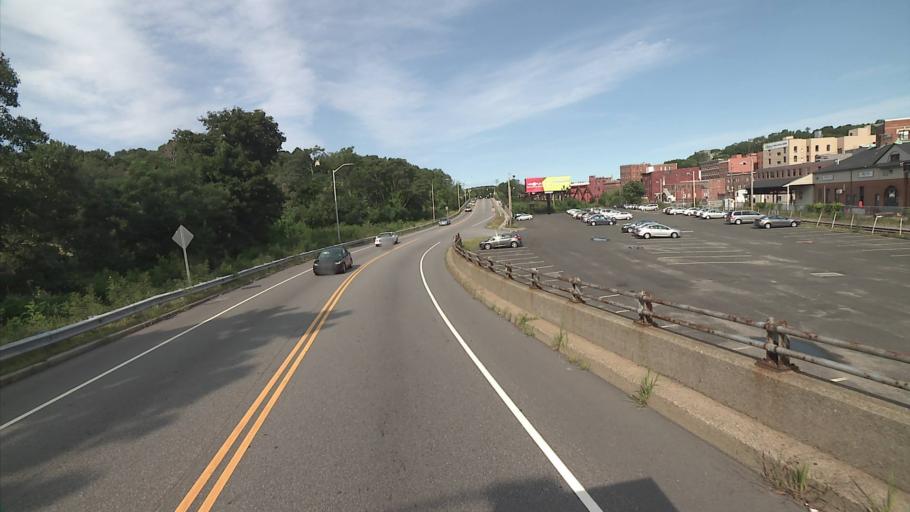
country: US
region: Connecticut
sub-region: New London County
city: Norwich
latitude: 41.5232
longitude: -72.0721
